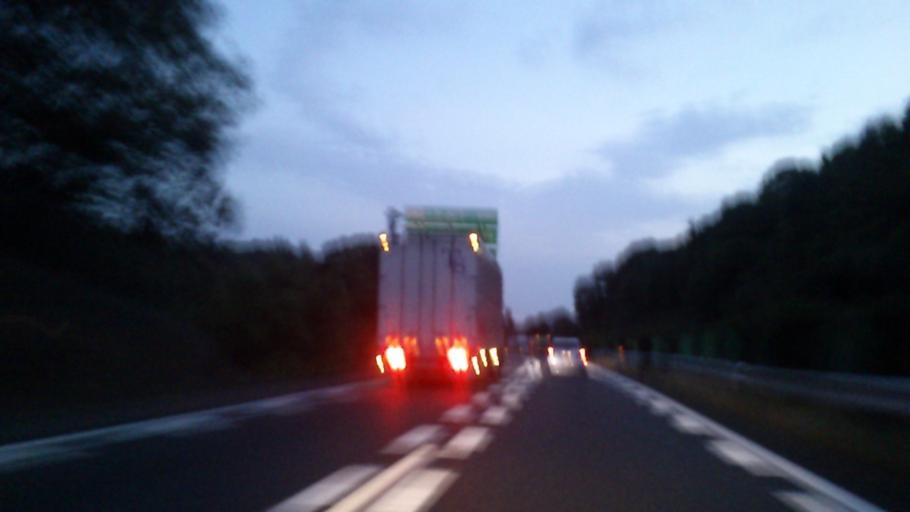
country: JP
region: Aichi
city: Kasugai
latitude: 35.3230
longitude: 137.0217
